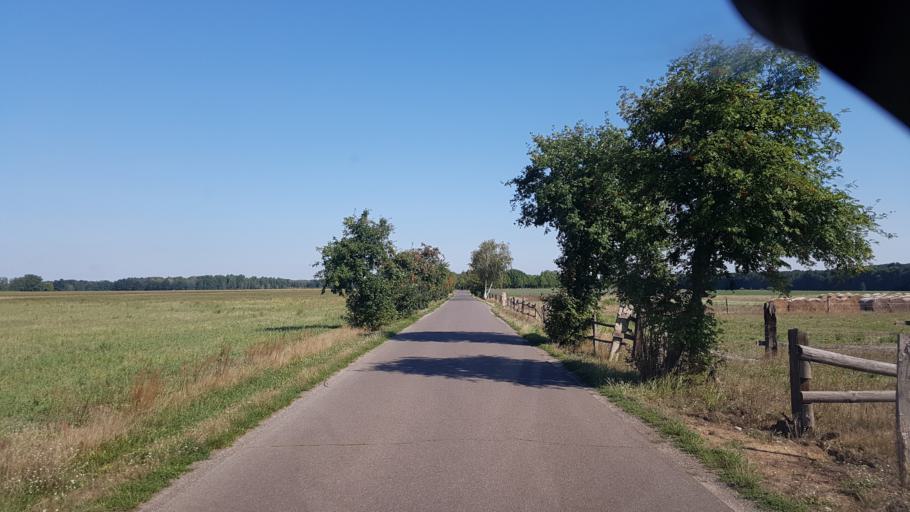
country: DE
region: Brandenburg
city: Vetschau
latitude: 51.7516
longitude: 14.0385
